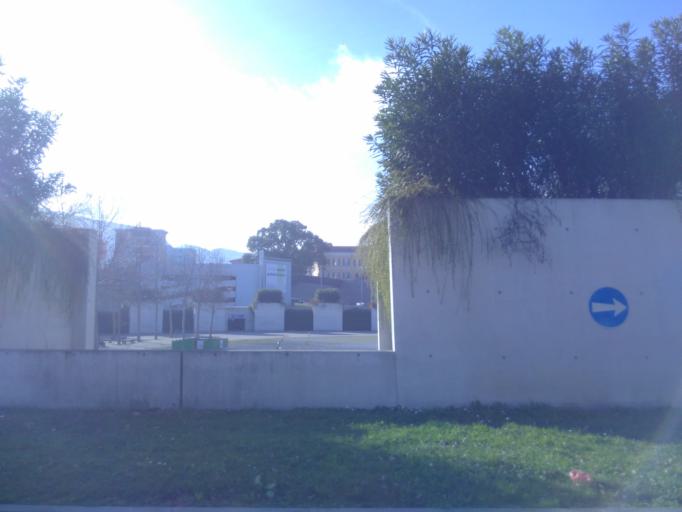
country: CH
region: Ticino
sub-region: Locarno District
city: Locarno
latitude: 46.1666
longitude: 8.7941
